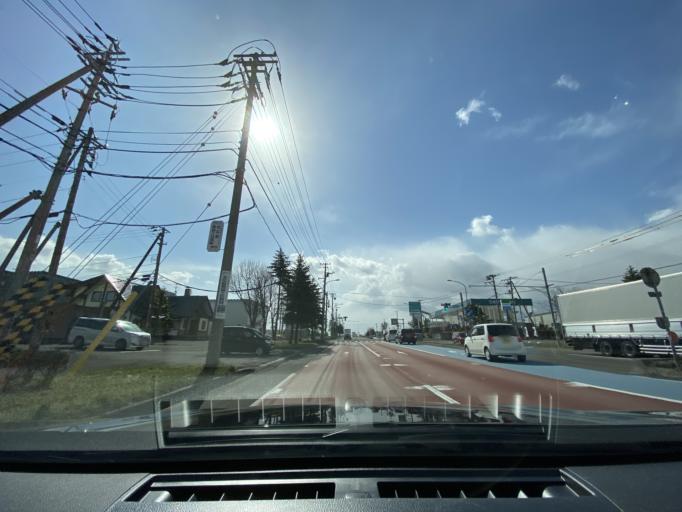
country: JP
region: Hokkaido
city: Kitahiroshima
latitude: 42.9640
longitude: 141.4881
